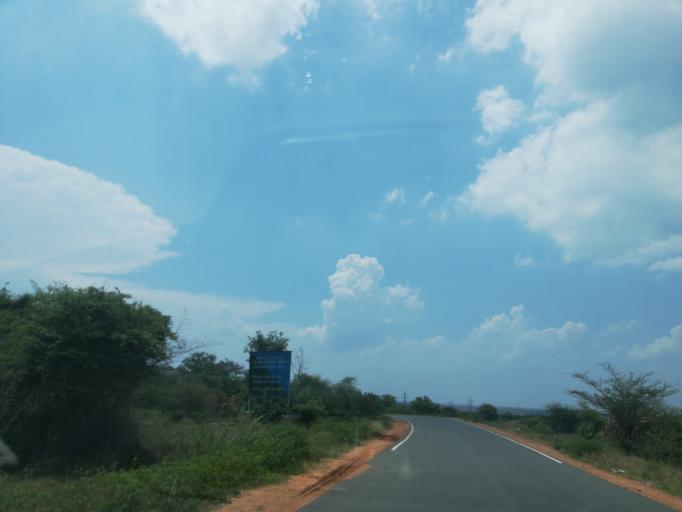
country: IN
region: Andhra Pradesh
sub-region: Guntur
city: Macherla
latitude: 16.5683
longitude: 79.3445
